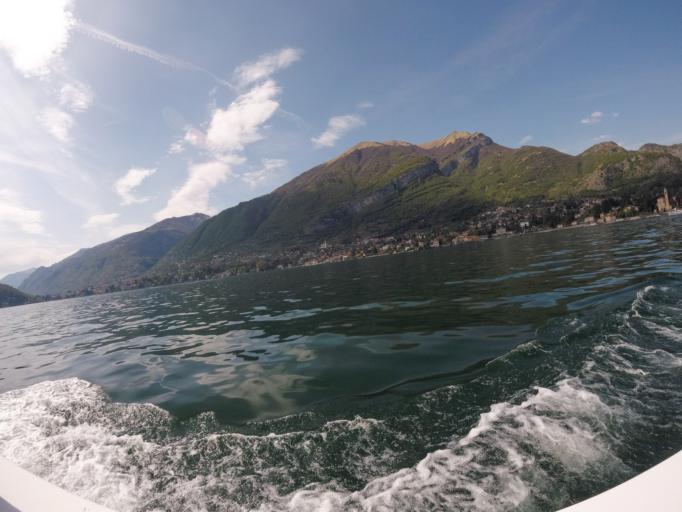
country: IT
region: Lombardy
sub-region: Provincia di Como
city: Tremezzo
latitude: 45.9754
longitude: 9.2187
